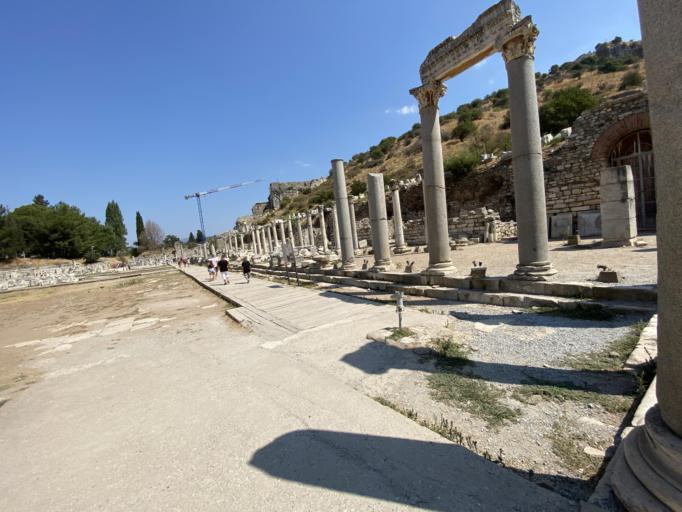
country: TR
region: Izmir
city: Selcuk
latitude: 37.9394
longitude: 27.3411
